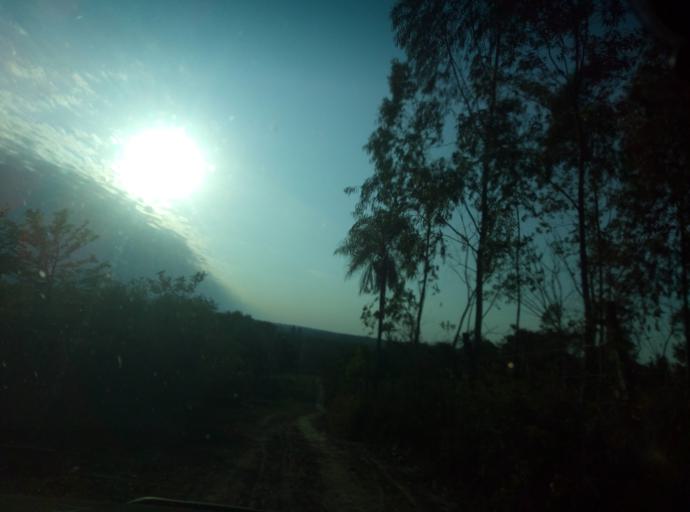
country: PY
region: Caaguazu
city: Doctor Cecilio Baez
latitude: -25.1987
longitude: -56.1300
